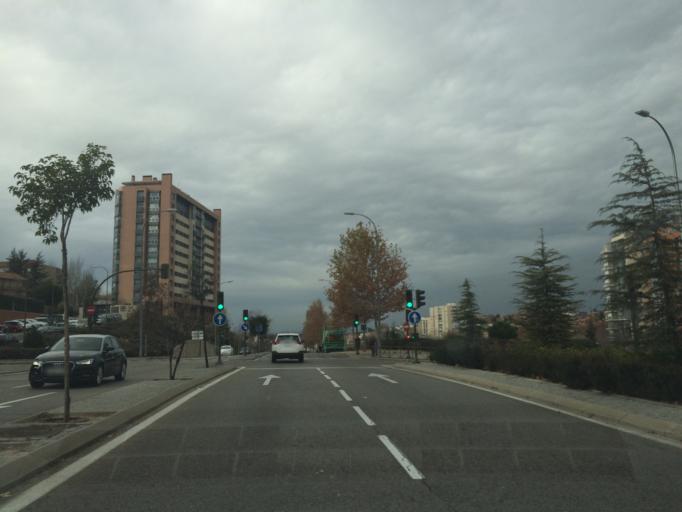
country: ES
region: Madrid
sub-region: Provincia de Madrid
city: Tetuan de las Victorias
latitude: 40.4719
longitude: -3.7224
